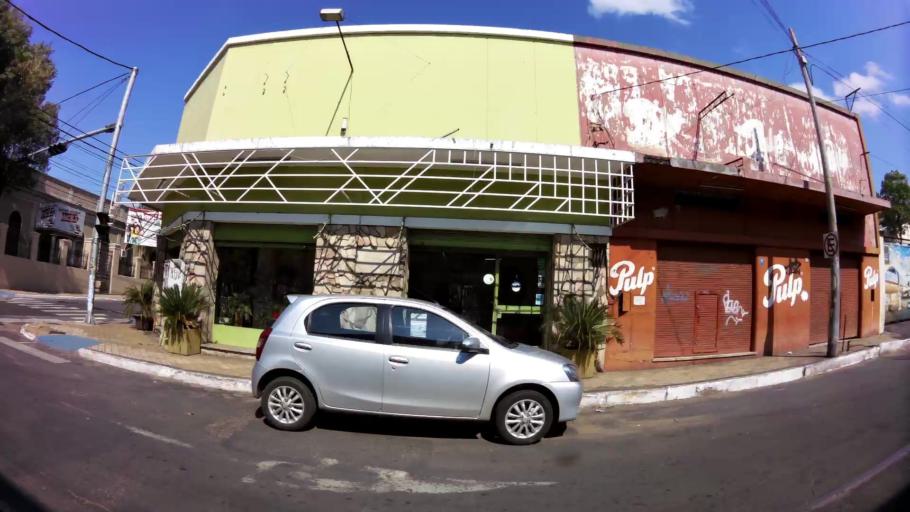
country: PY
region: Asuncion
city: Asuncion
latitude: -25.2861
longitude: -57.6254
